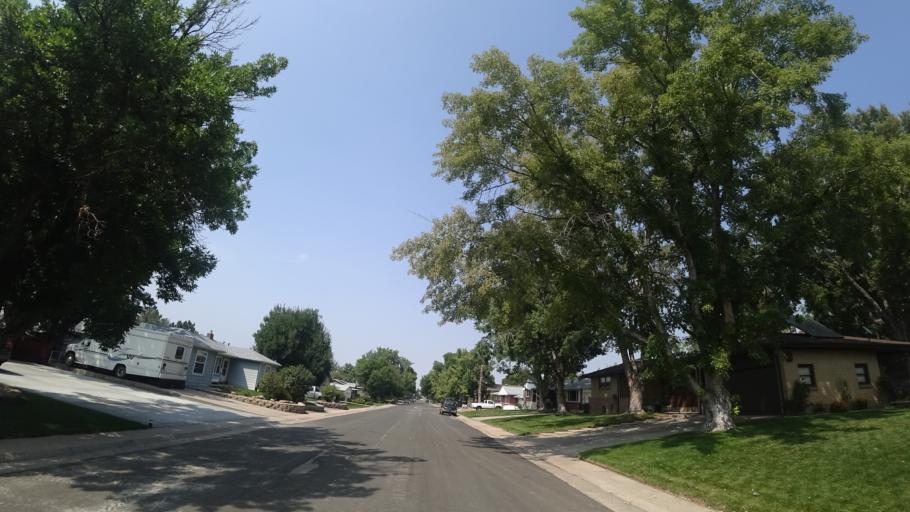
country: US
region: Colorado
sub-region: Arapahoe County
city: Littleton
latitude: 39.6303
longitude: -105.0019
